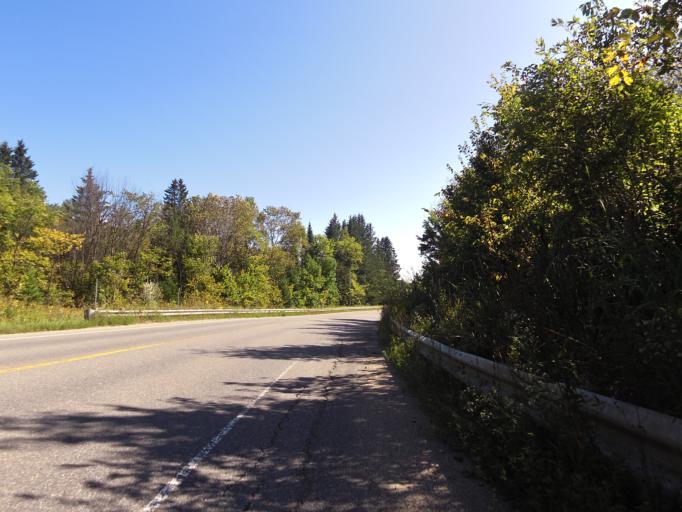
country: CA
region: Ontario
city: Clarence-Rockland
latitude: 45.6551
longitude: -75.4430
